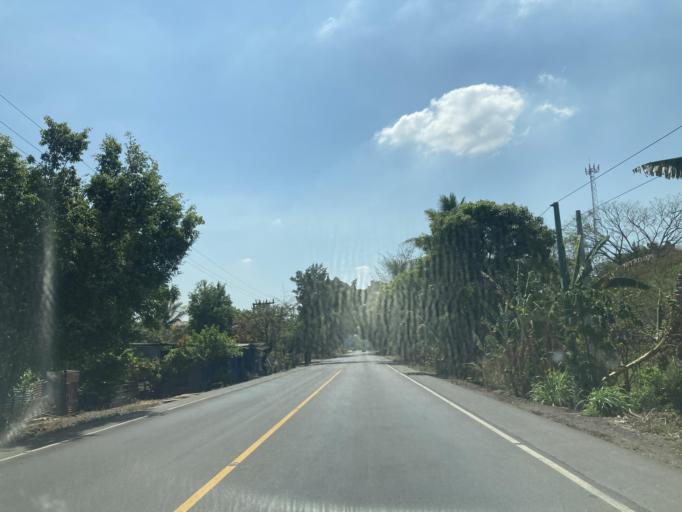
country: GT
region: Escuintla
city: Guanagazapa
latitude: 14.2038
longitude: -90.7141
